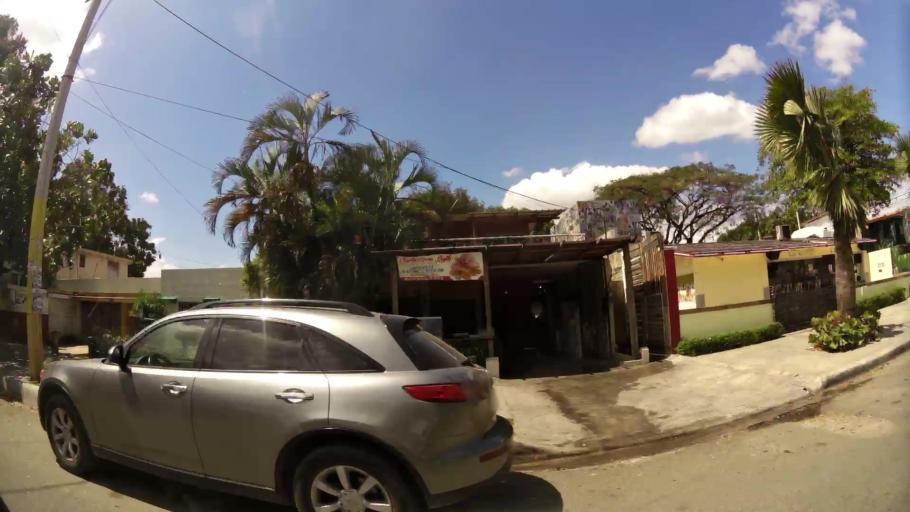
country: DO
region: San Cristobal
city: San Cristobal
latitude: 18.4145
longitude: -70.1066
